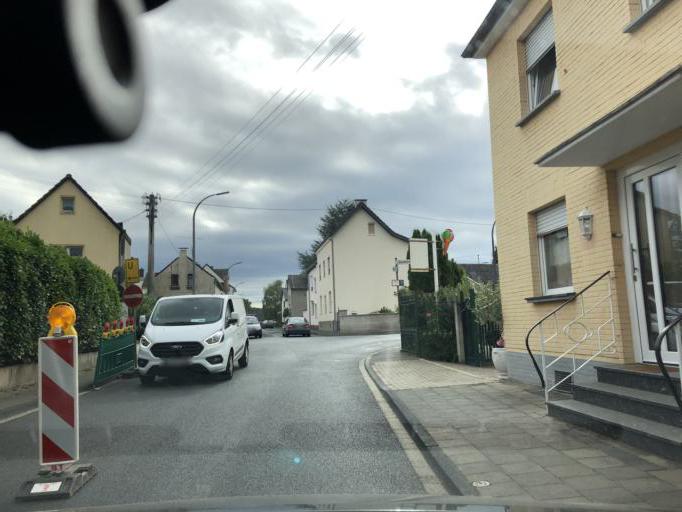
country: DE
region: North Rhine-Westphalia
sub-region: Regierungsbezirk Koln
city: Bonn
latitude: 50.7743
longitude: 7.0890
